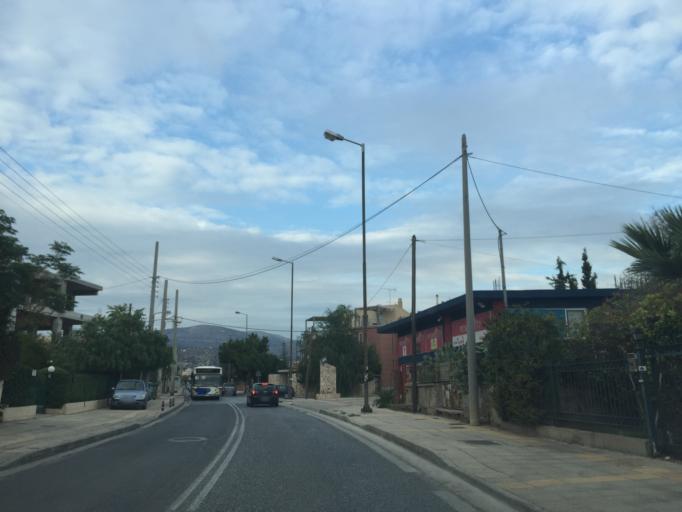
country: GR
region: Attica
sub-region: Nomarchia Anatolikis Attikis
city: Vari
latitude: 37.8242
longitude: 23.8042
